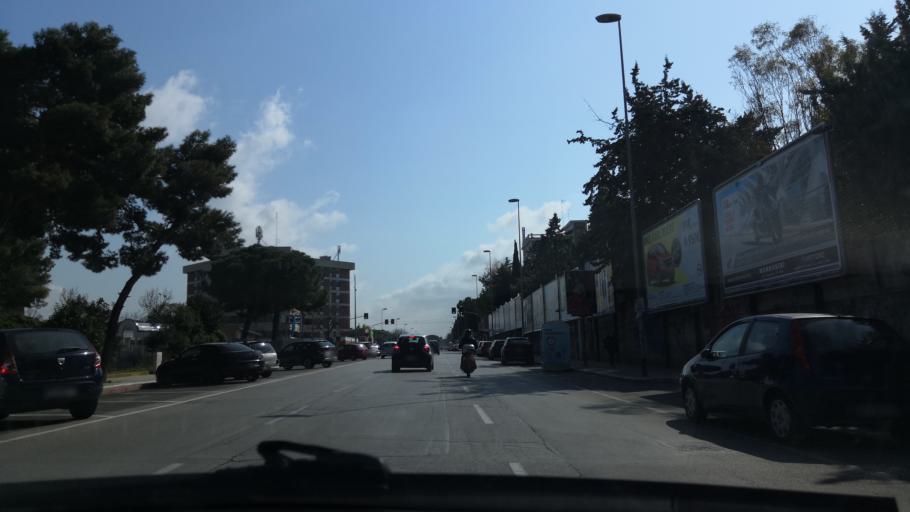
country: IT
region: Apulia
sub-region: Provincia di Bari
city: Bari
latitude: 41.1018
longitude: 16.8736
